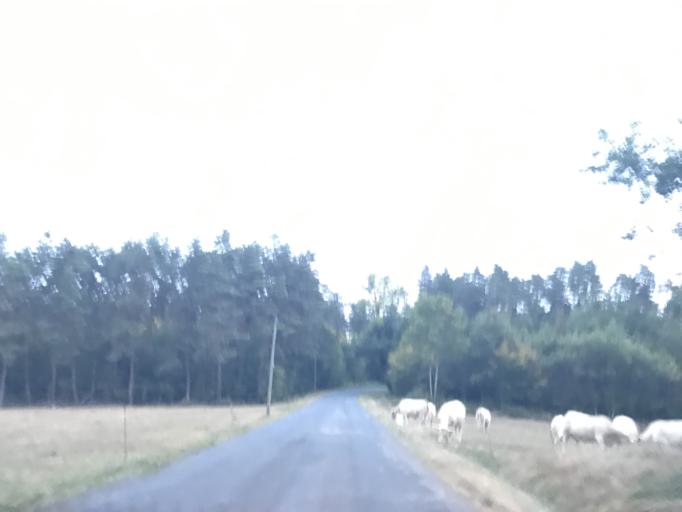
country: FR
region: Auvergne
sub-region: Departement du Puy-de-Dome
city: Escoutoux
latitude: 45.7978
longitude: 3.5653
